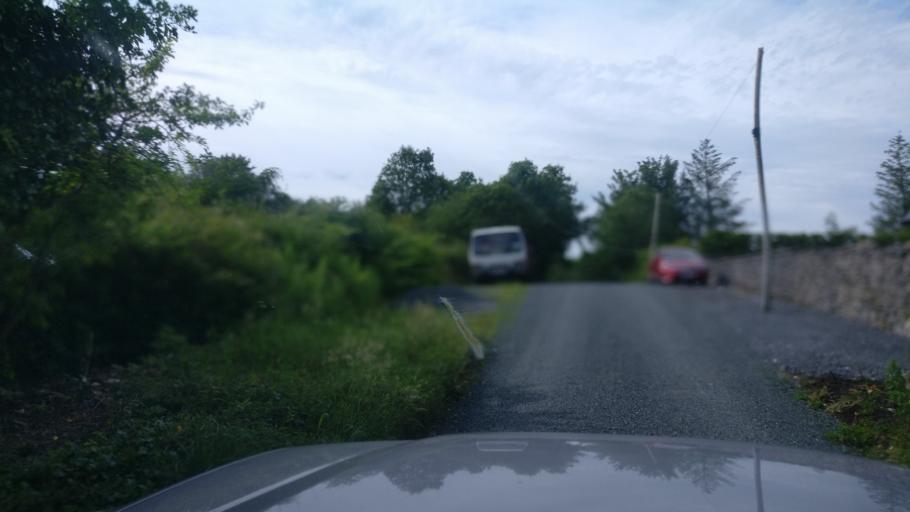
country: IE
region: Connaught
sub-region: County Galway
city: Gort
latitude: 53.1076
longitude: -8.7154
